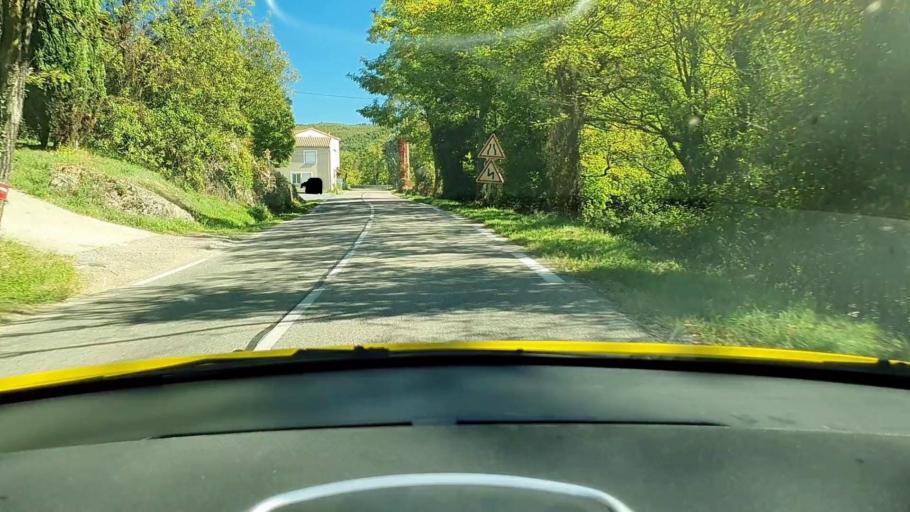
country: FR
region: Languedoc-Roussillon
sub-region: Departement du Gard
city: Aveze
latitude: 43.9707
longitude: 3.5728
